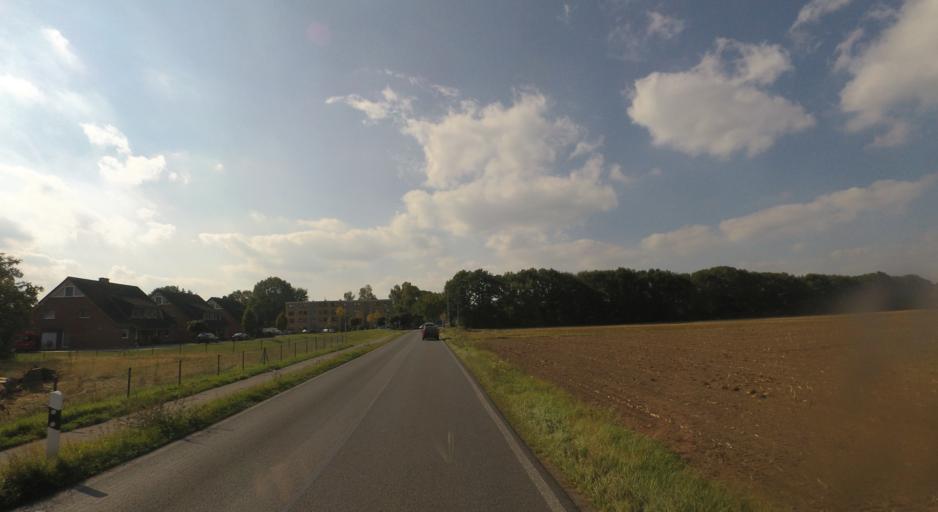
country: DE
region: North Rhine-Westphalia
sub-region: Regierungsbezirk Dusseldorf
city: Wesel
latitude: 51.6705
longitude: 6.6562
